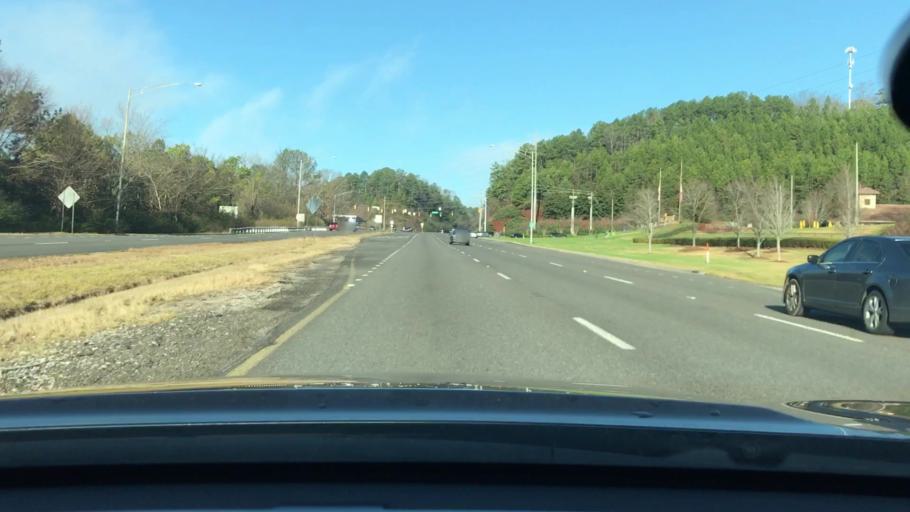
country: US
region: Alabama
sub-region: Jefferson County
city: Cahaba Heights
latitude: 33.4438
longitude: -86.7327
